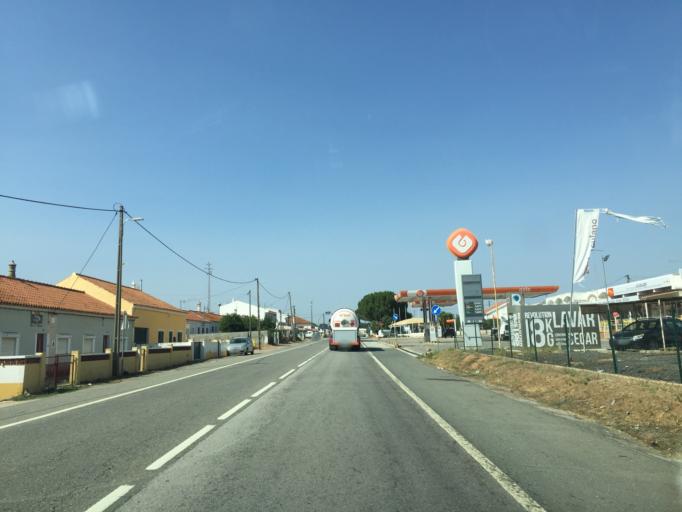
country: PT
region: Beja
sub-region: Aljustrel
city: Aljustrel
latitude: 37.9455
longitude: -8.3806
